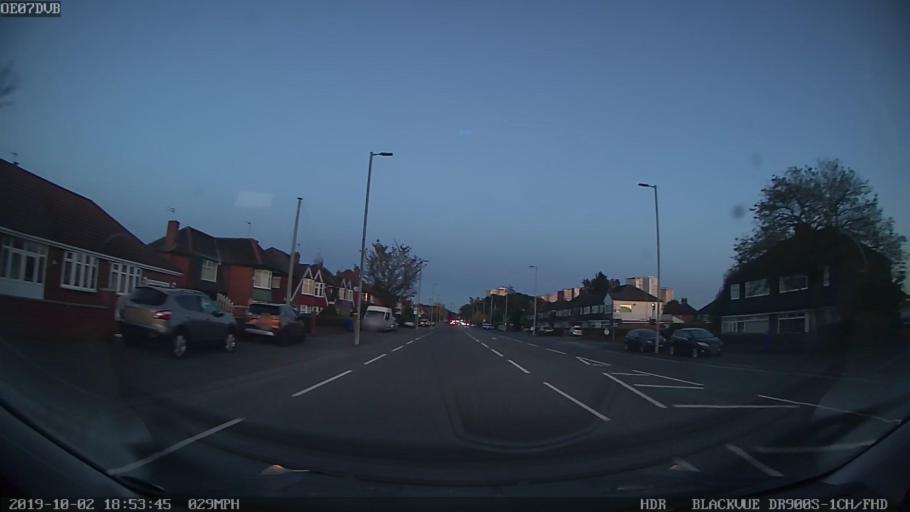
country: GB
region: England
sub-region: Borough of Rochdale
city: Middleton
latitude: 53.5308
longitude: -2.1993
